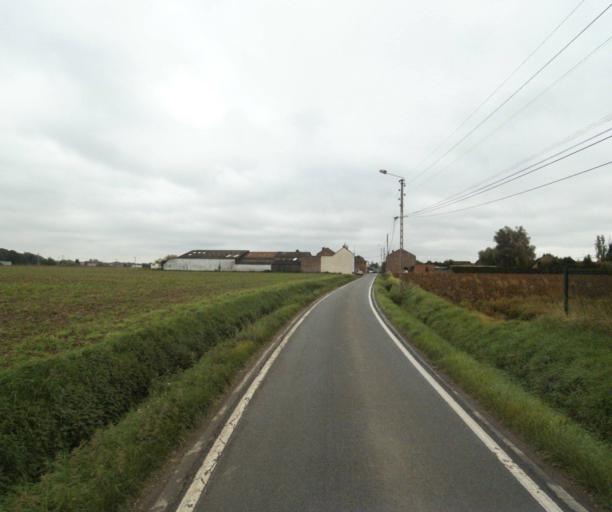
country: FR
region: Nord-Pas-de-Calais
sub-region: Departement du Nord
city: Santes
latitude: 50.5899
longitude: 2.9516
